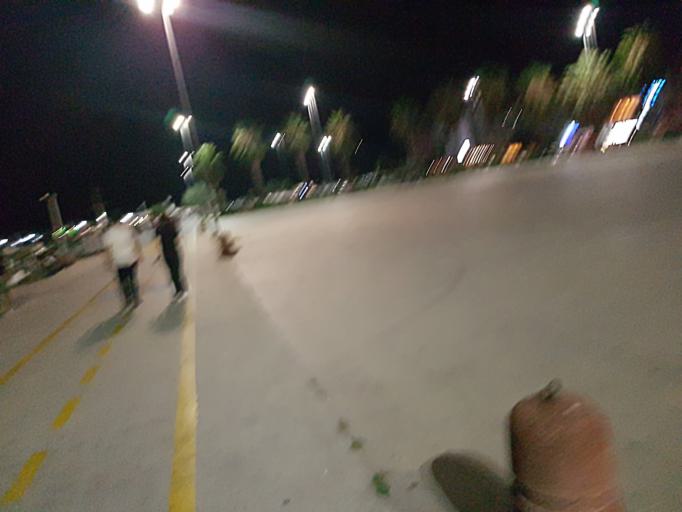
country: TR
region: Istanbul
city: Bahcelievler
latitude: 40.9564
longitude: 28.8223
